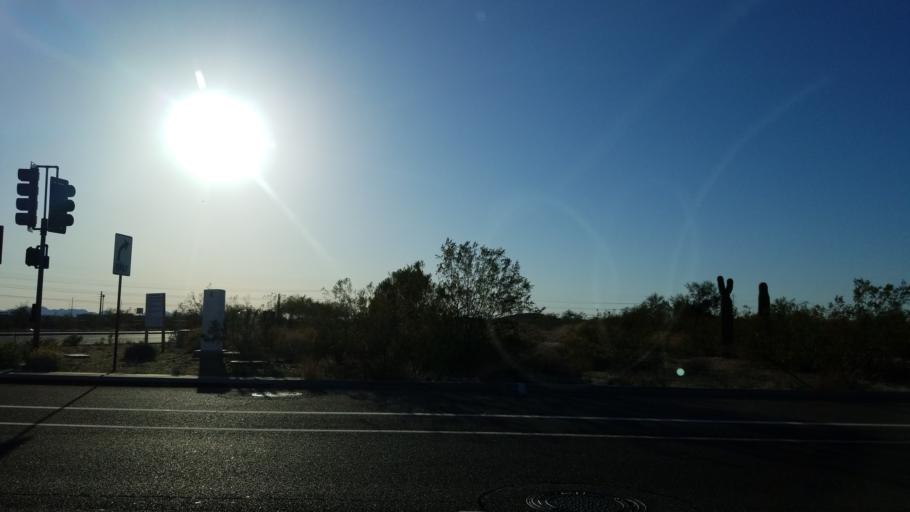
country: US
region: Arizona
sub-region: Maricopa County
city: Paradise Valley
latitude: 33.6547
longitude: -111.8874
